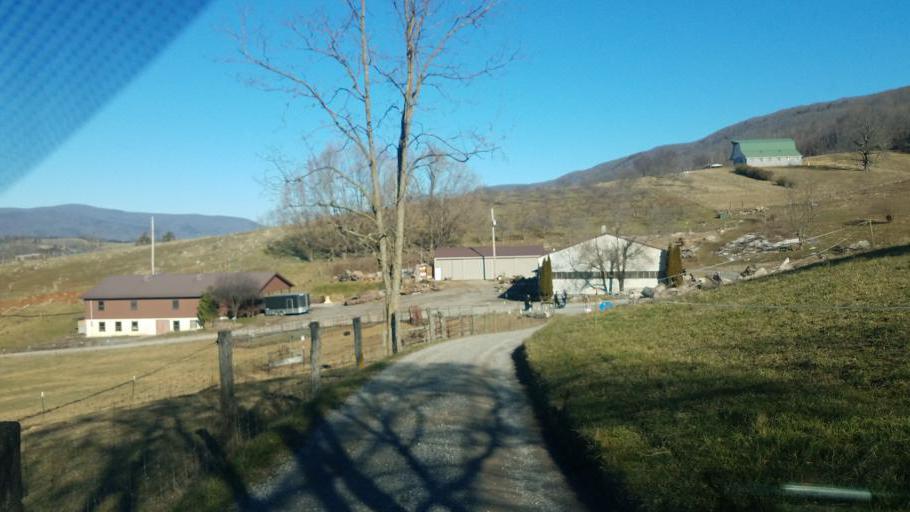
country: US
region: Virginia
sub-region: Pulaski County
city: Pulaski
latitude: 37.1541
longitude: -80.8626
